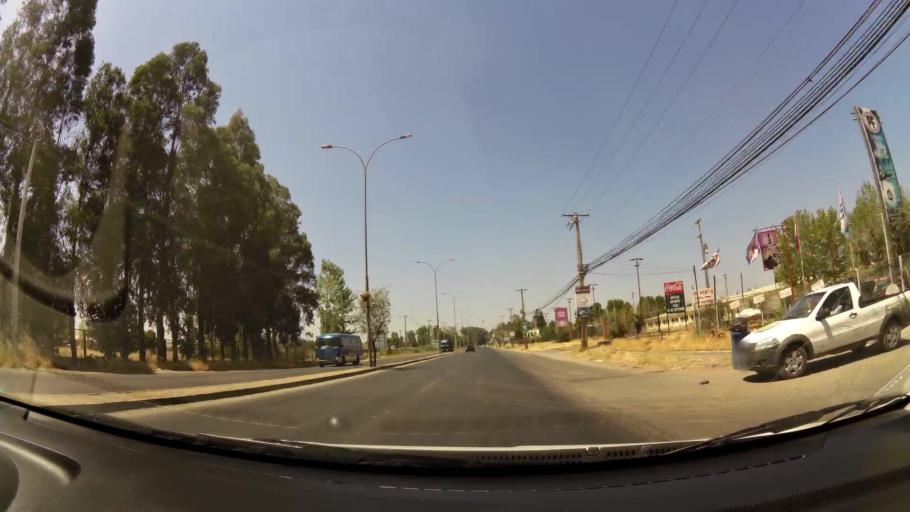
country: CL
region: Maule
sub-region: Provincia de Talca
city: Talca
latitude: -35.4379
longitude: -71.6184
